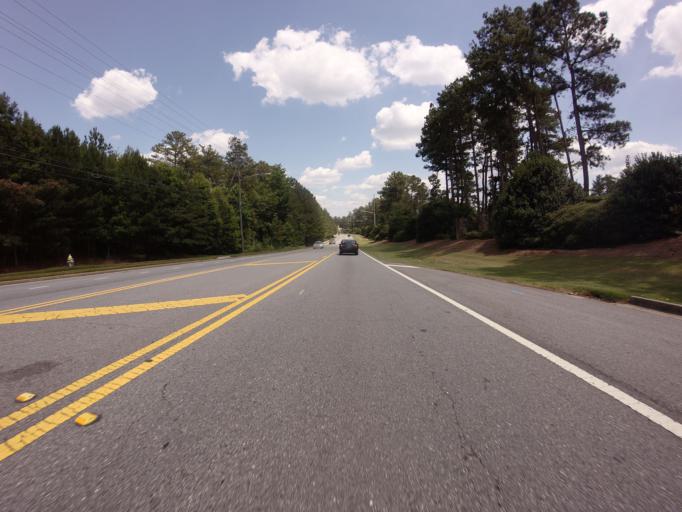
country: US
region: Georgia
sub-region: Fulton County
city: Johns Creek
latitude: 34.0168
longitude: -84.2386
